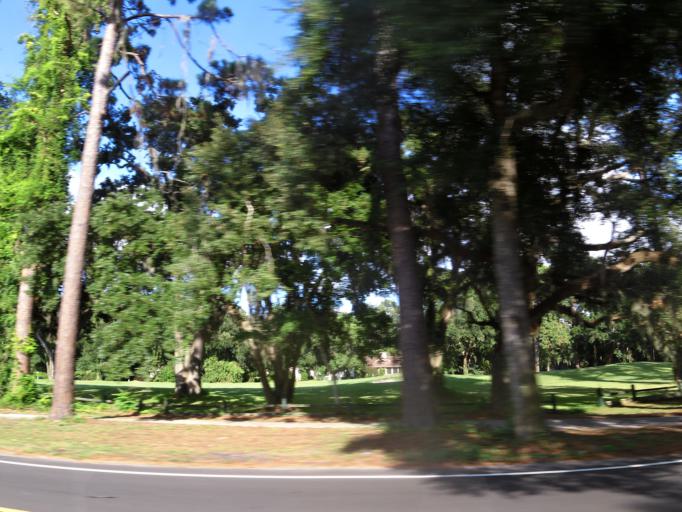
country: US
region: Georgia
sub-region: Glynn County
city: Saint Simon Mills
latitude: 31.1900
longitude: -81.3767
